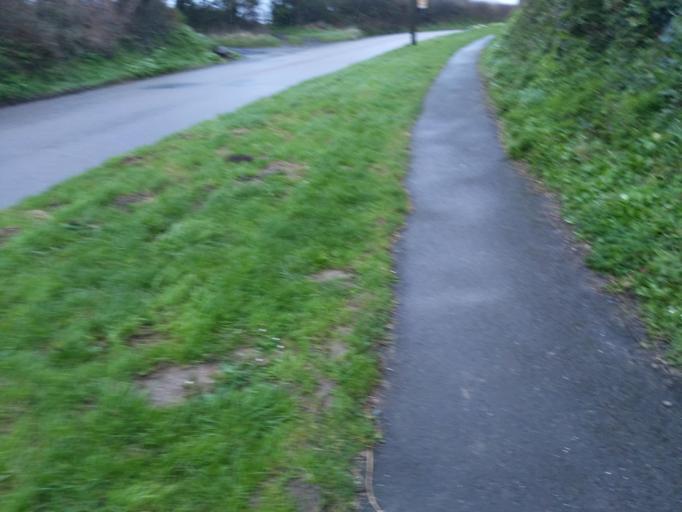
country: GB
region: England
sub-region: Devon
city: Wembury
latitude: 50.3205
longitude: -4.0346
